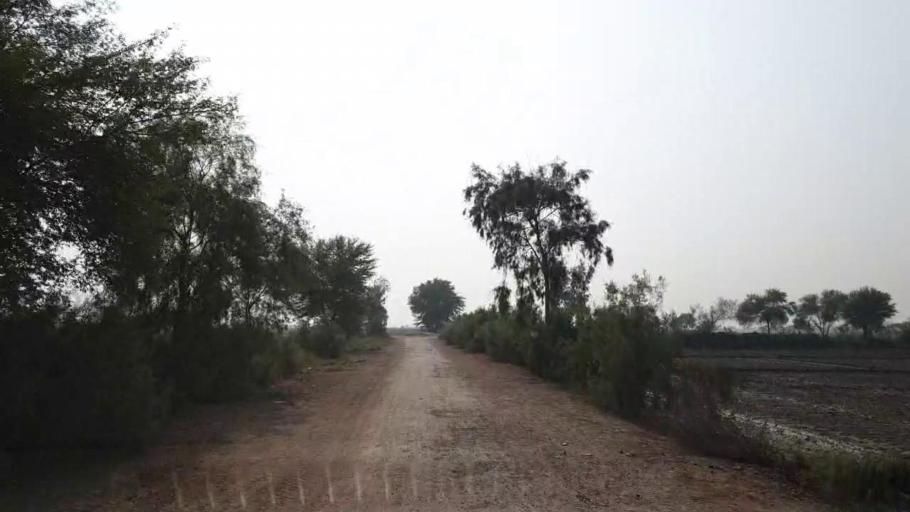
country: PK
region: Sindh
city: Bhan
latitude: 26.4654
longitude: 67.7393
